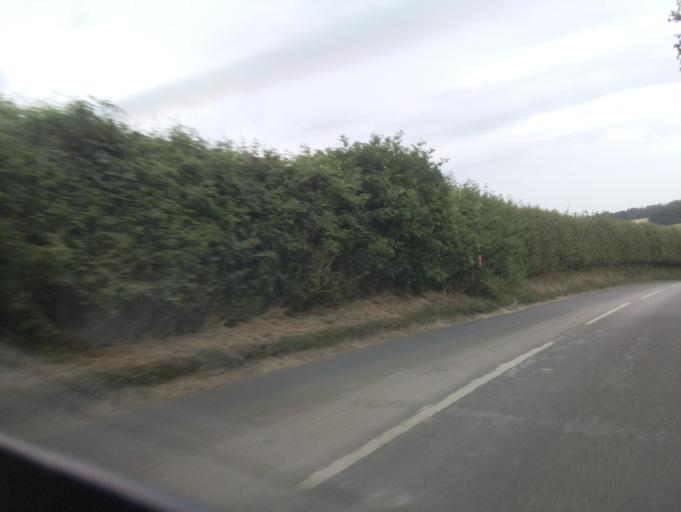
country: GB
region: England
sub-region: Dorset
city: Sherborne
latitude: 50.9274
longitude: -2.5395
